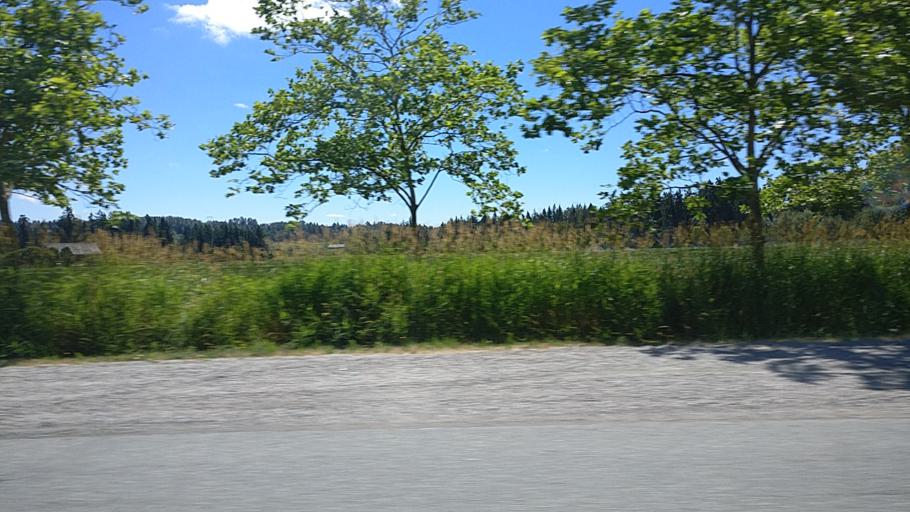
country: US
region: Washington
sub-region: Whatcom County
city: Blaine
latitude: 49.0167
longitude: -122.7288
